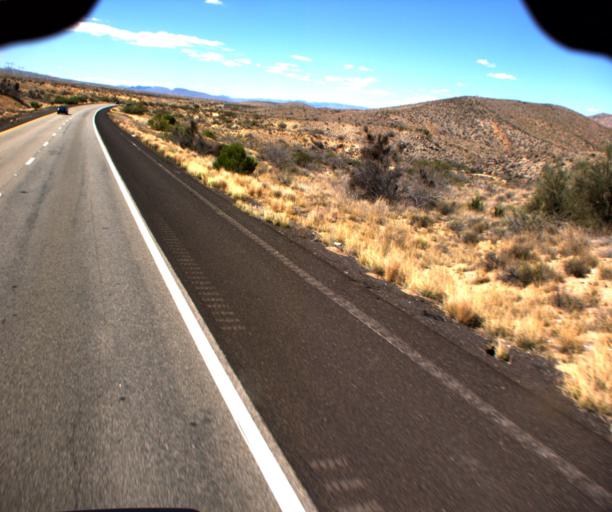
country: US
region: Arizona
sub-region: Mohave County
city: Kingman
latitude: 34.9626
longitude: -113.6699
